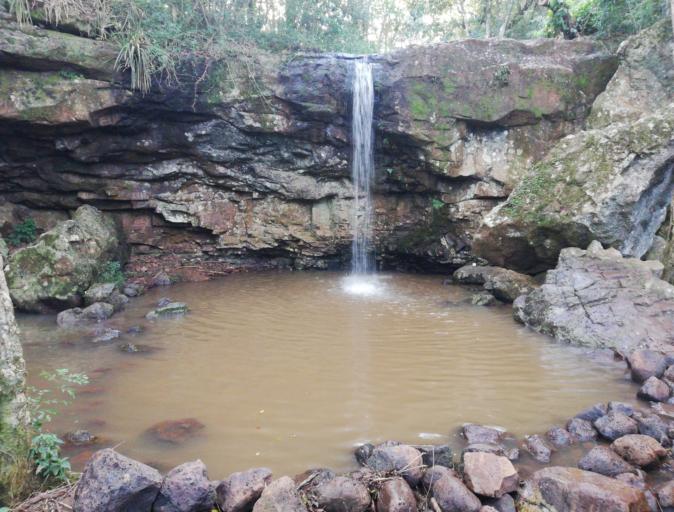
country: AR
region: Misiones
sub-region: Departamento de Candelaria
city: Candelaria
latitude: -27.4542
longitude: -55.7241
